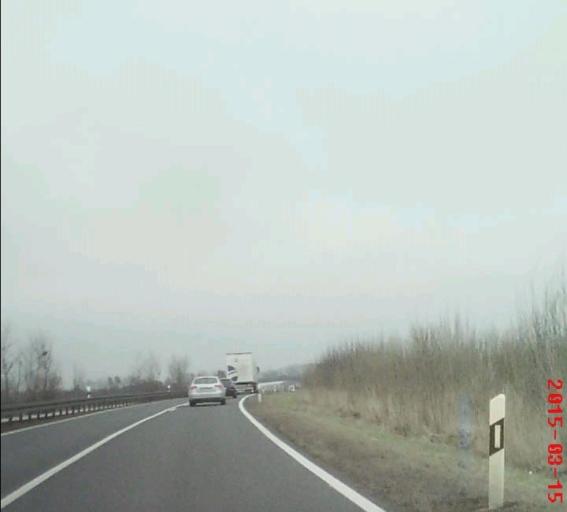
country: DE
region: Thuringia
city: Dollstadt
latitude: 51.0857
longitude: 10.7945
